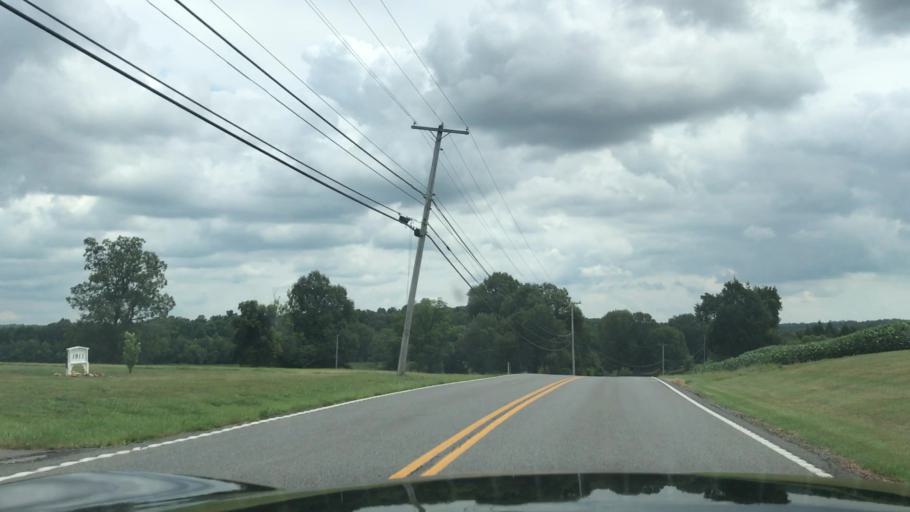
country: US
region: Kentucky
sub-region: Muhlenberg County
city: Greenville
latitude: 37.2050
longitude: -87.1466
